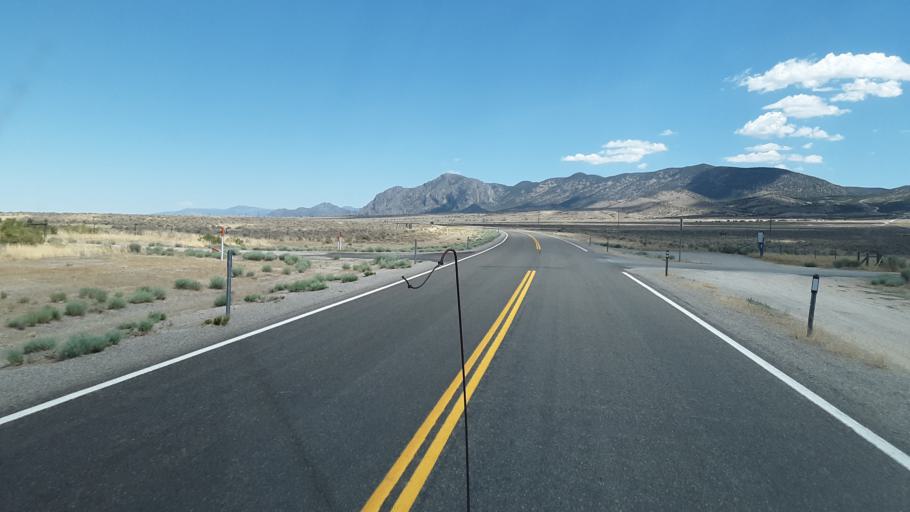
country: US
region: Nevada
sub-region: White Pine County
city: McGill
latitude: 39.0709
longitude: -114.4507
